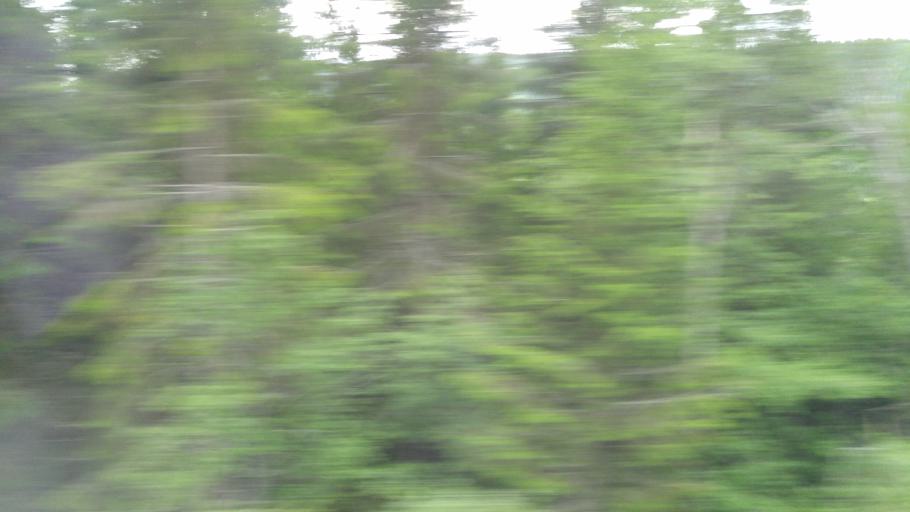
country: NO
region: Nord-Trondelag
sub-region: Meraker
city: Meraker
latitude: 63.4043
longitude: 11.7754
